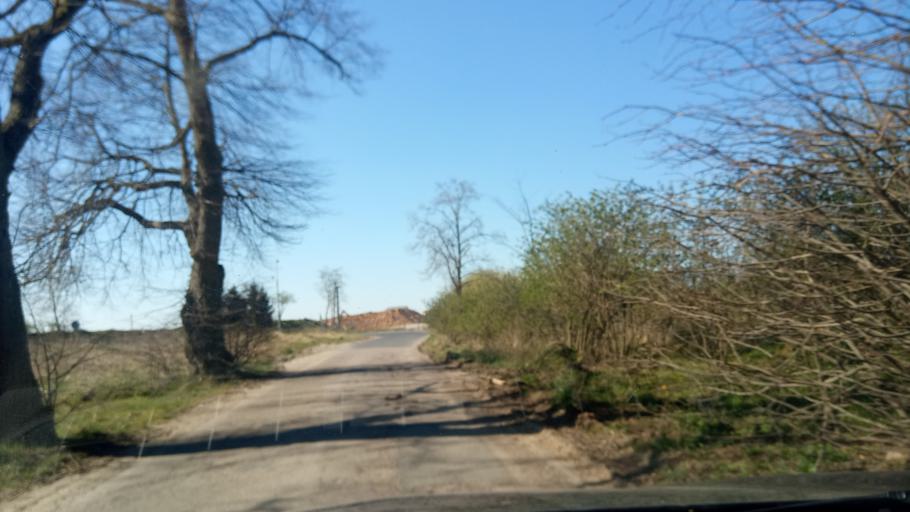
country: PL
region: West Pomeranian Voivodeship
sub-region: Powiat szczecinecki
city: Szczecinek
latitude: 53.6949
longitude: 16.7213
